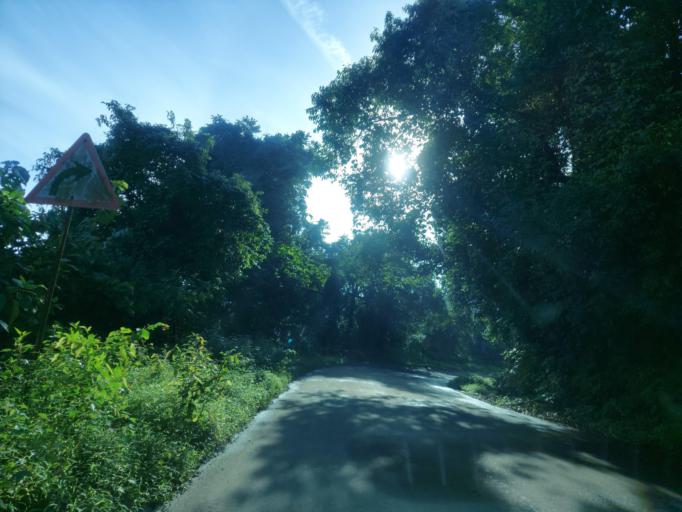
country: IN
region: Maharashtra
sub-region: Sindhudurg
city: Savantvadi
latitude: 15.9347
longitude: 73.9751
